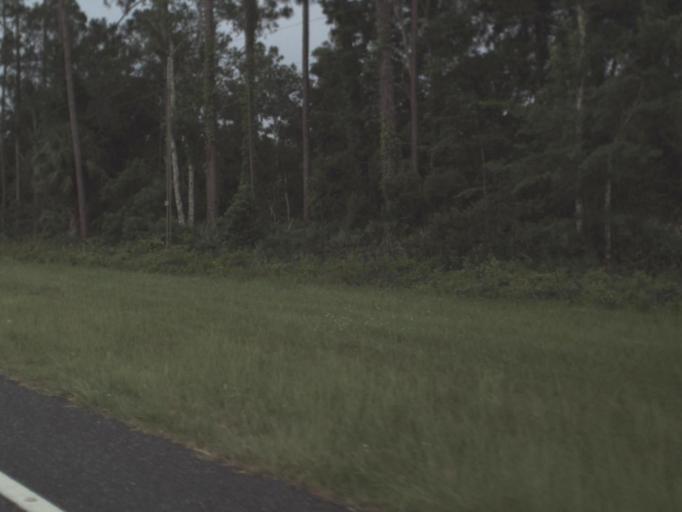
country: US
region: Florida
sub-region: Levy County
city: Inglis
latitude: 29.1685
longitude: -82.6467
